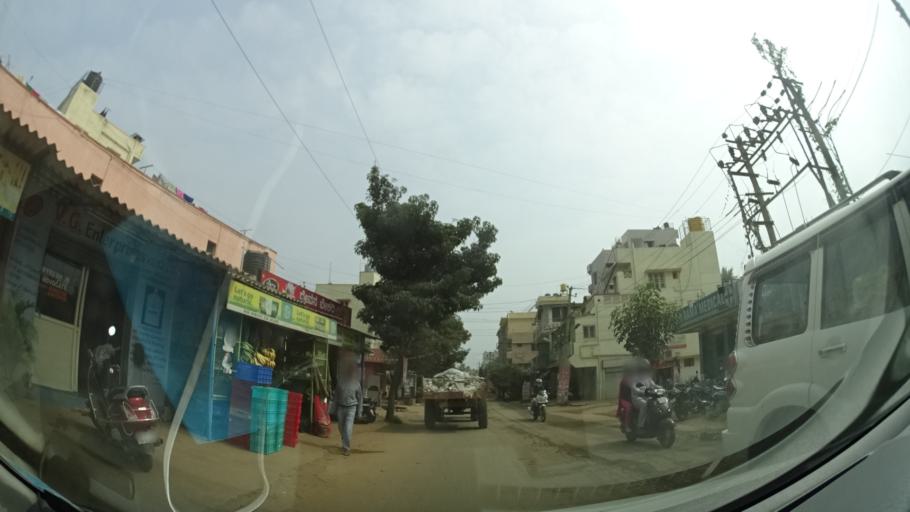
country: IN
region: Karnataka
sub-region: Bangalore Rural
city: Hoskote
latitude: 12.9643
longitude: 77.7538
